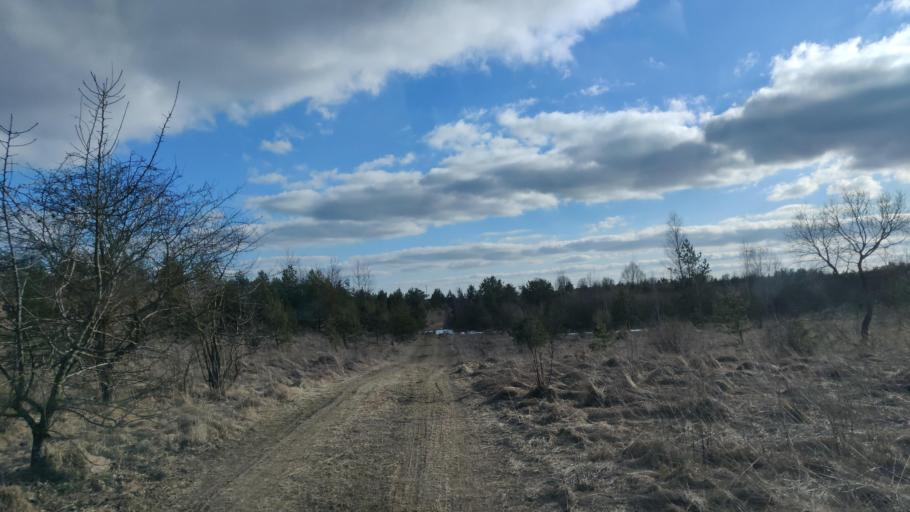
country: LT
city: Lentvaris
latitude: 54.6131
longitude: 24.9993
